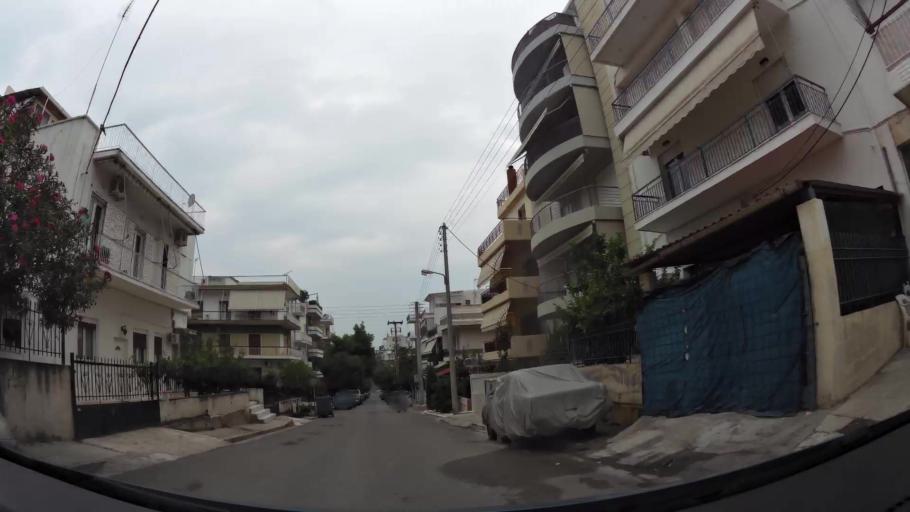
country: GR
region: Attica
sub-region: Nomarchia Athinas
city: Palaio Faliro
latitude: 37.9269
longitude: 23.7162
